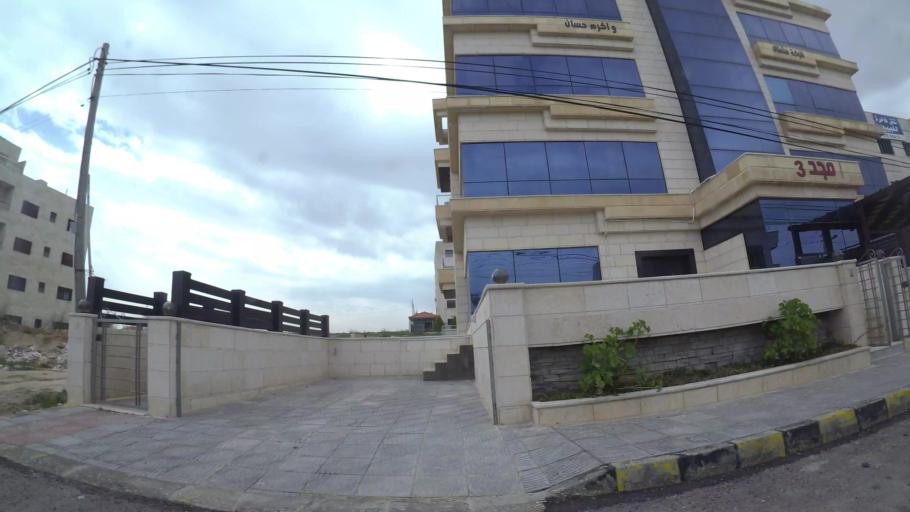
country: JO
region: Amman
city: Umm as Summaq
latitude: 31.9108
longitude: 35.8393
